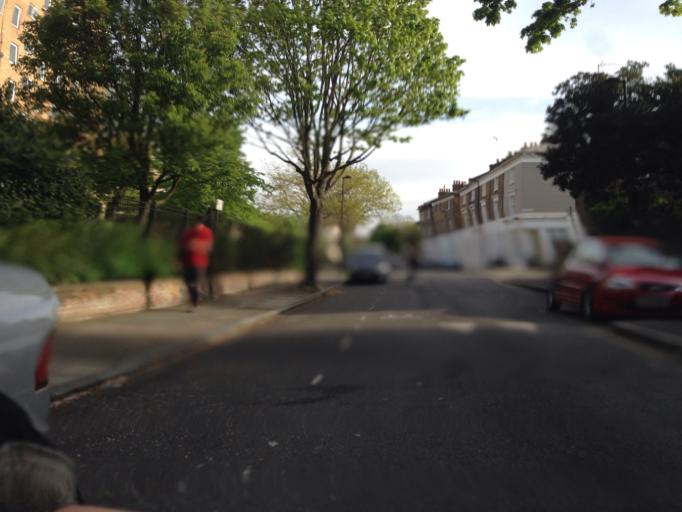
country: GB
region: England
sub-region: Greater London
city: Brixton
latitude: 51.4756
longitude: -0.1279
